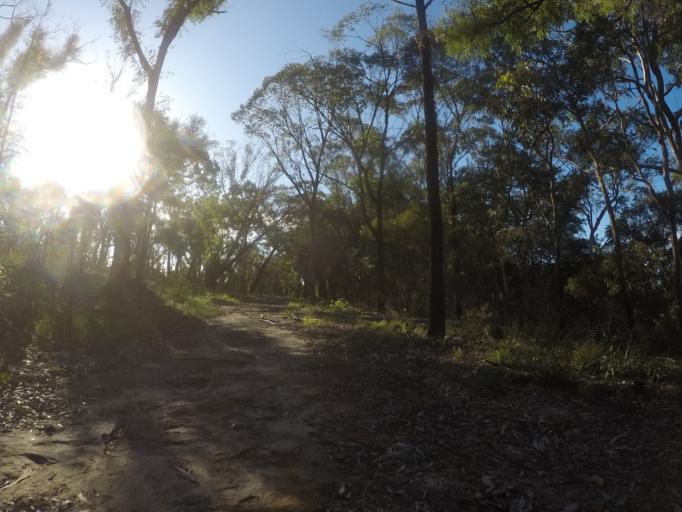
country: AU
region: New South Wales
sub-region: Hornsby Shire
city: Glenorie
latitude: -33.3504
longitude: 151.0007
